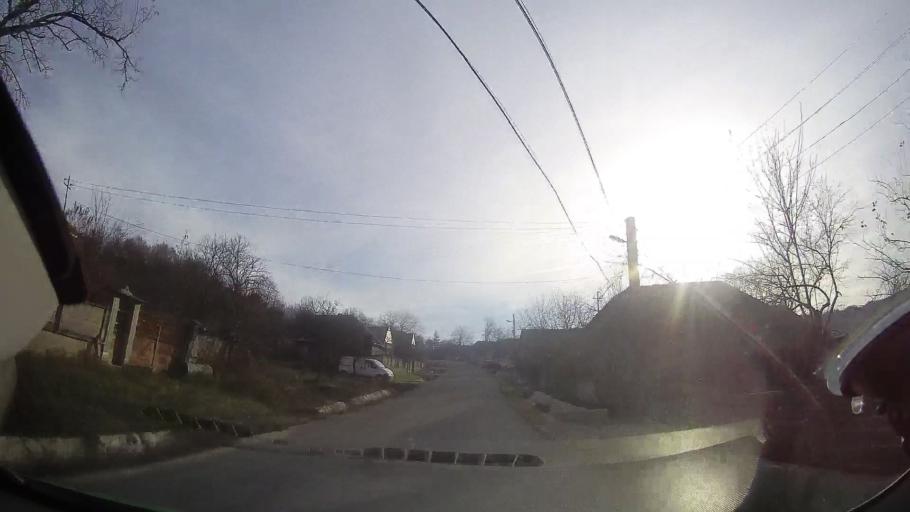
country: RO
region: Bihor
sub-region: Comuna Sarbi
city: Burzuc
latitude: 47.1753
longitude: 22.1529
